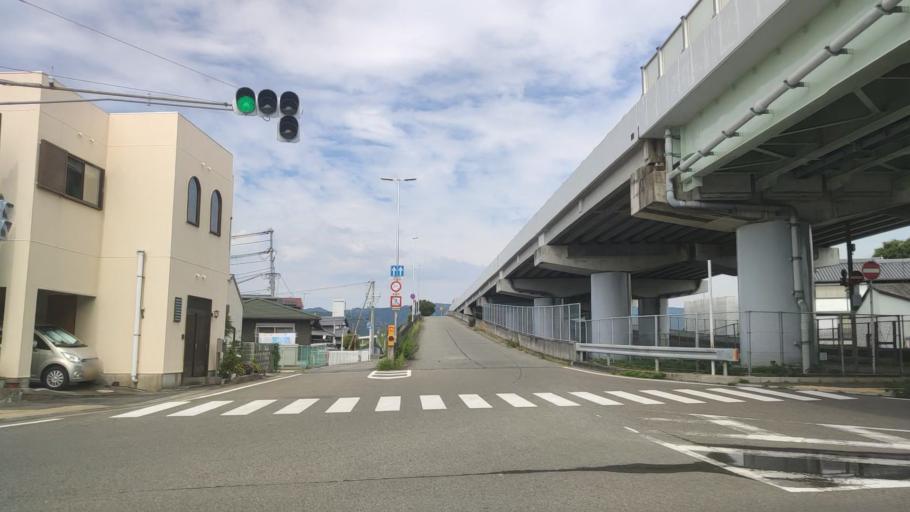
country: JP
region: Wakayama
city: Wakayama-shi
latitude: 34.2453
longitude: 135.2179
